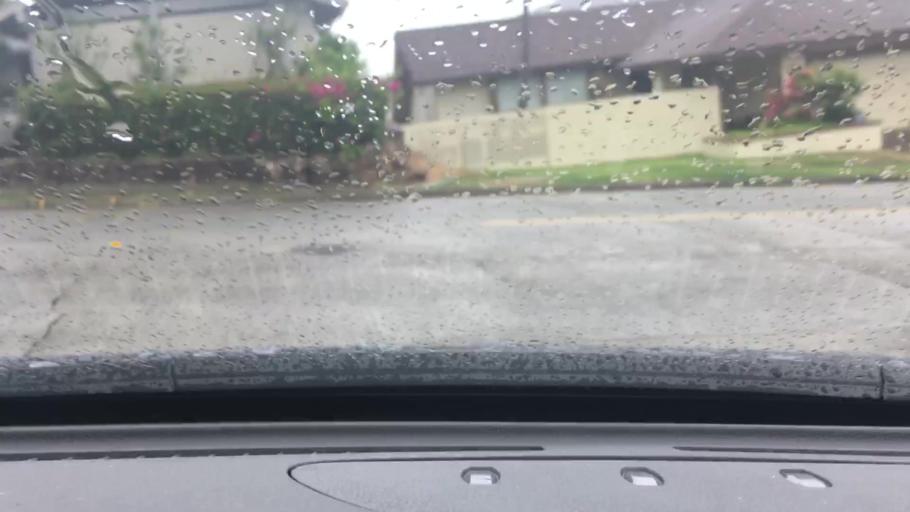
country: US
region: Hawaii
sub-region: Honolulu County
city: Waimanalo Beach
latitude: 21.2940
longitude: -157.7024
